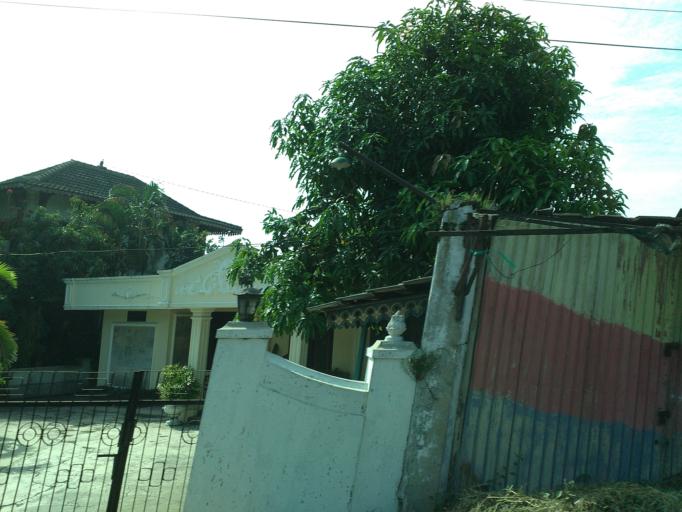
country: ID
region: Central Java
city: Ceper
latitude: -7.6654
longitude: 110.6649
